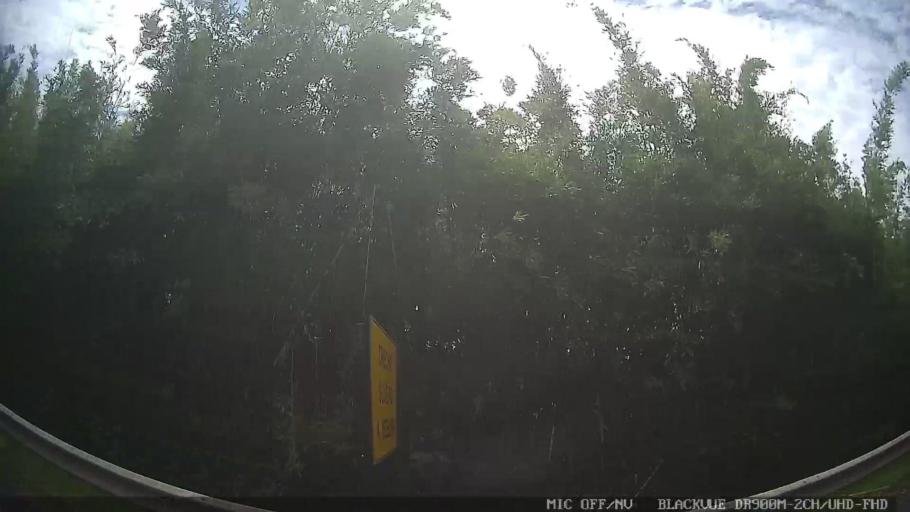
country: BR
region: Sao Paulo
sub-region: Laranjal Paulista
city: Laranjal Paulista
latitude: -23.0557
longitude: -47.8229
